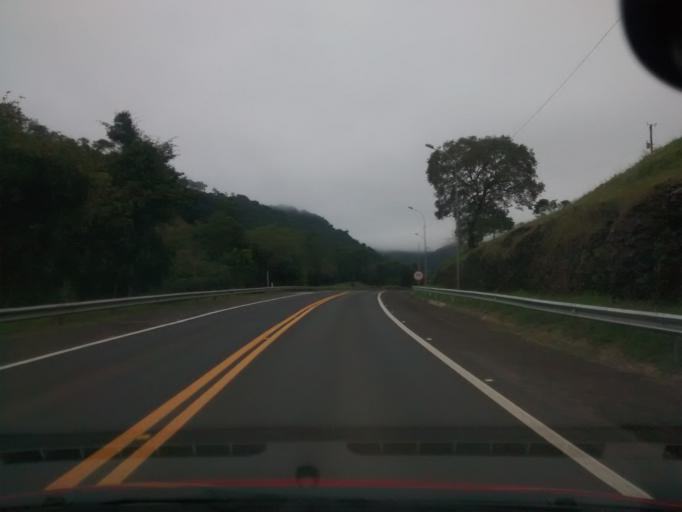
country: BR
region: Rio Grande do Sul
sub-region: Vacaria
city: Estrela
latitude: -28.2054
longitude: -50.7590
